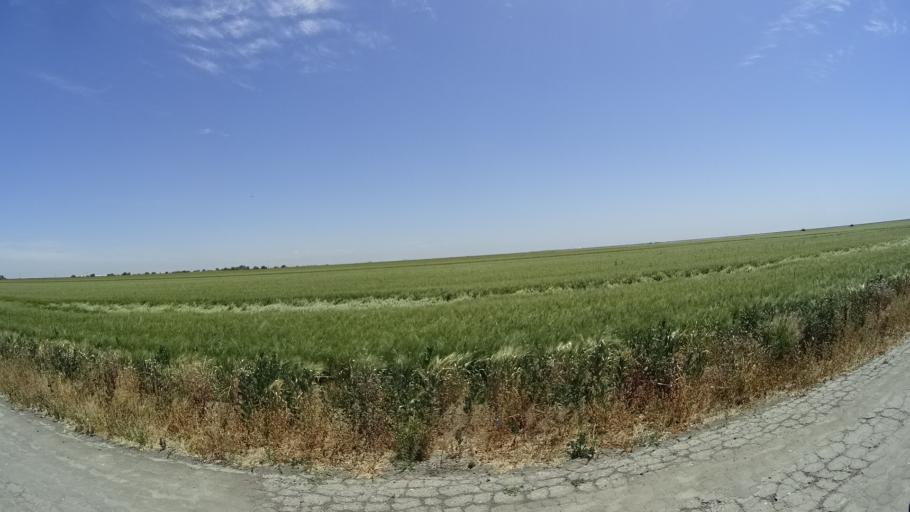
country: US
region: California
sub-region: Kings County
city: Stratford
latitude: 36.1315
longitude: -119.7340
